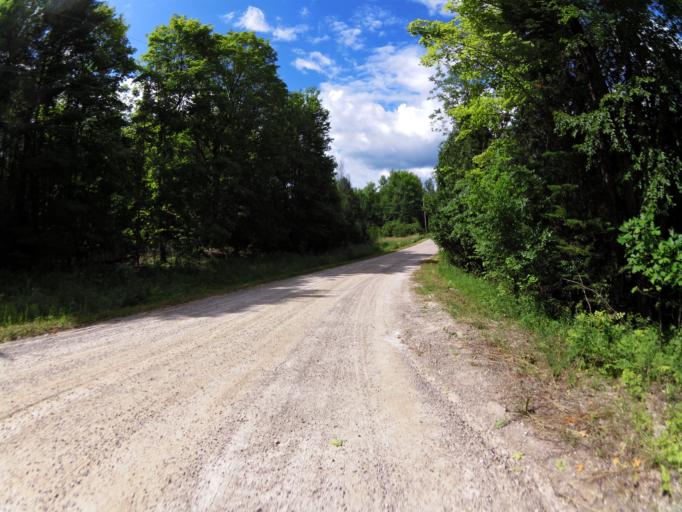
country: CA
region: Ontario
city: Perth
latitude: 45.0344
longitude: -76.4977
